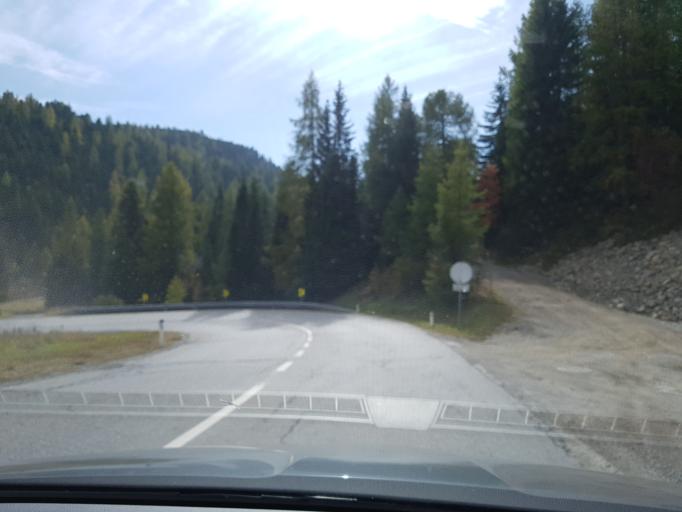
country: AT
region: Carinthia
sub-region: Politischer Bezirk Spittal an der Drau
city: Kleinkirchheim
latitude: 46.9305
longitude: 13.8720
